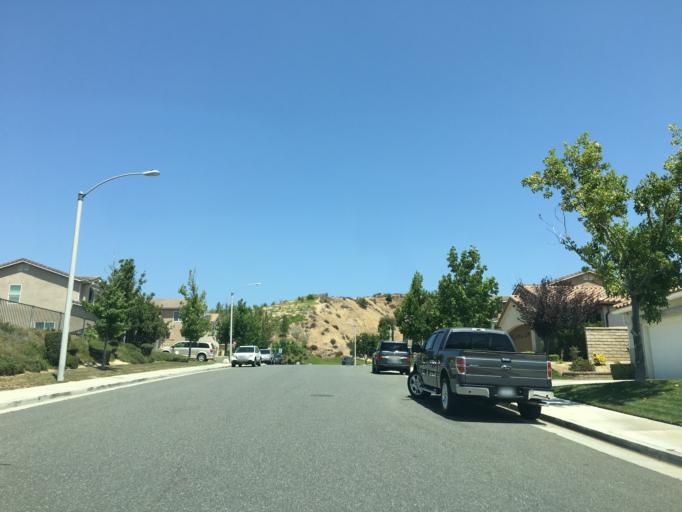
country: US
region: California
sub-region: Los Angeles County
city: Valencia
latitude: 34.4539
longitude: -118.6297
